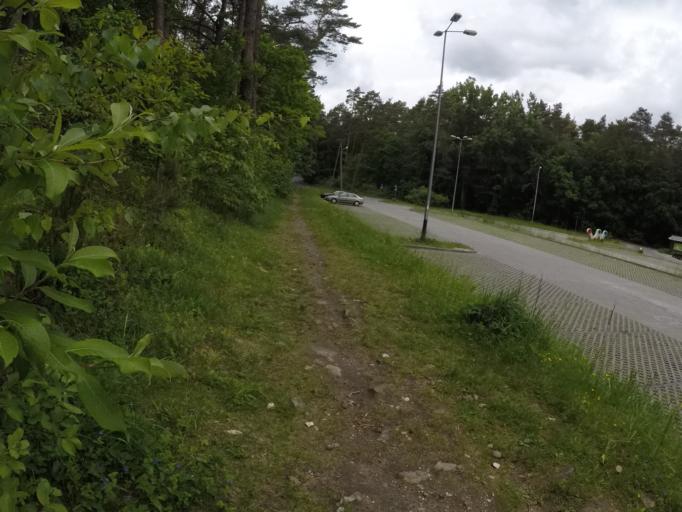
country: PL
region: Swietokrzyskie
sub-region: Powiat kielecki
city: Kielce
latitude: 50.8411
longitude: 20.6079
